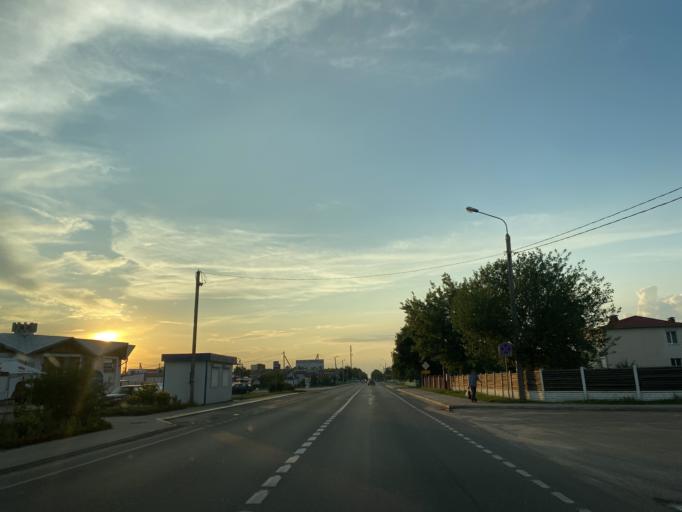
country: BY
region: Brest
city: Ivatsevichy
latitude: 52.7086
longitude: 25.3547
